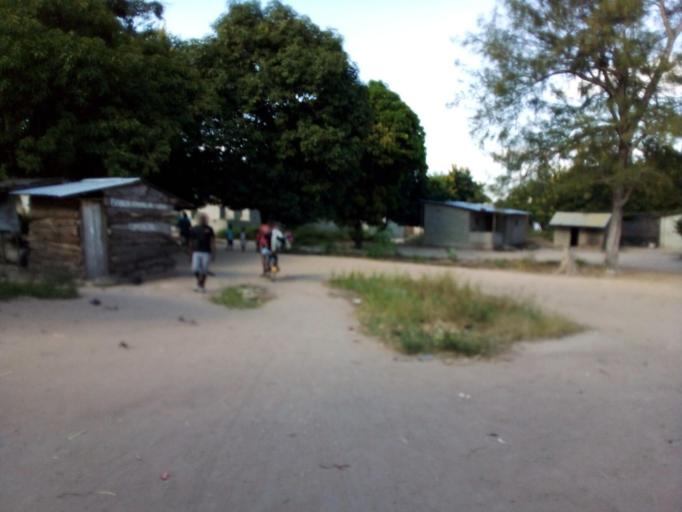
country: MZ
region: Zambezia
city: Quelimane
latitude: -17.6040
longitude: 36.8213
